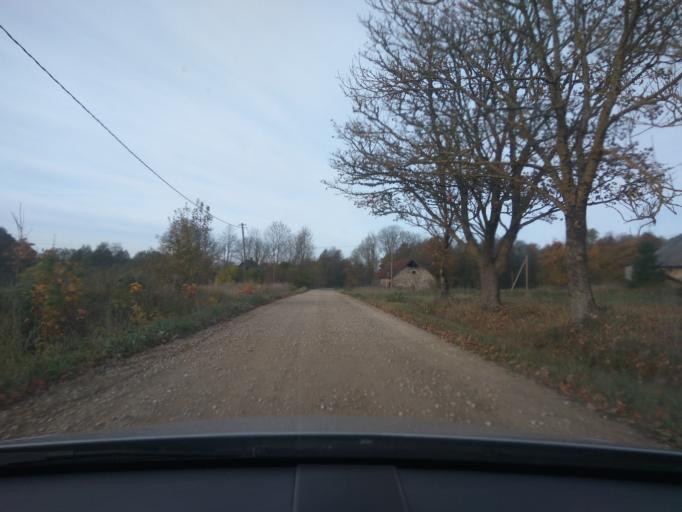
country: LV
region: Alsunga
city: Alsunga
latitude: 56.8752
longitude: 21.6808
